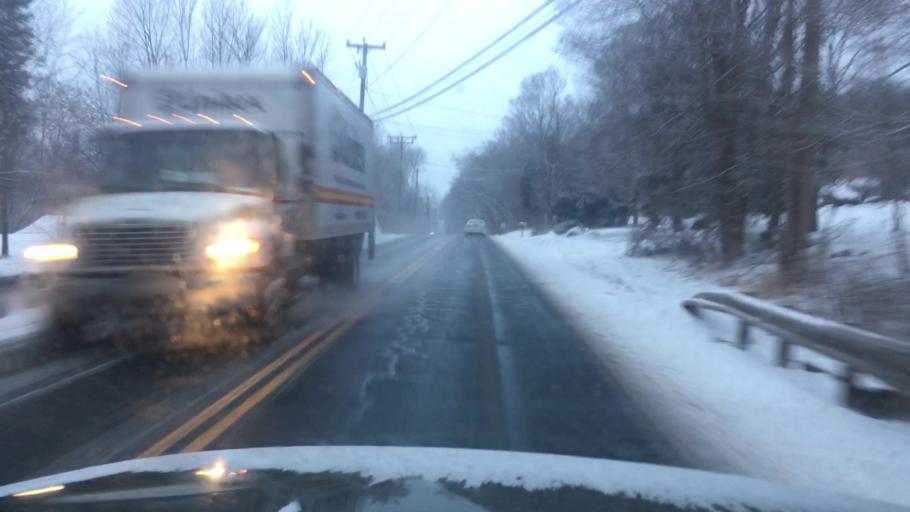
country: US
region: Connecticut
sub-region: Tolland County
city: Somers
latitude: 41.9823
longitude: -72.4131
